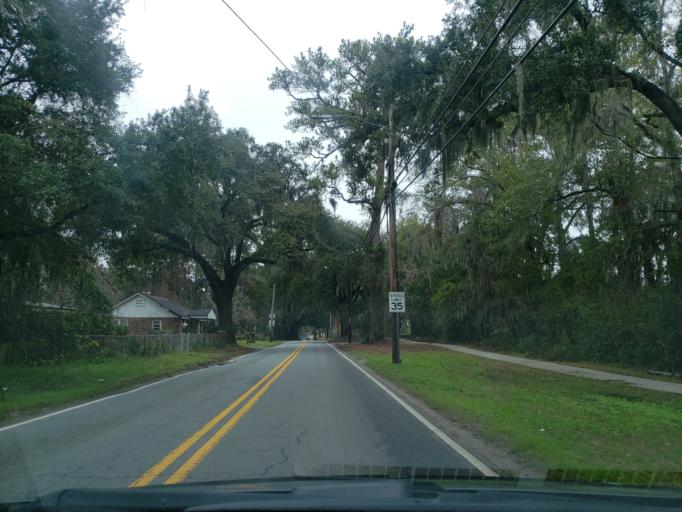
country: US
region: Georgia
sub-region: Chatham County
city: Montgomery
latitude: 31.9510
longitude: -81.1459
